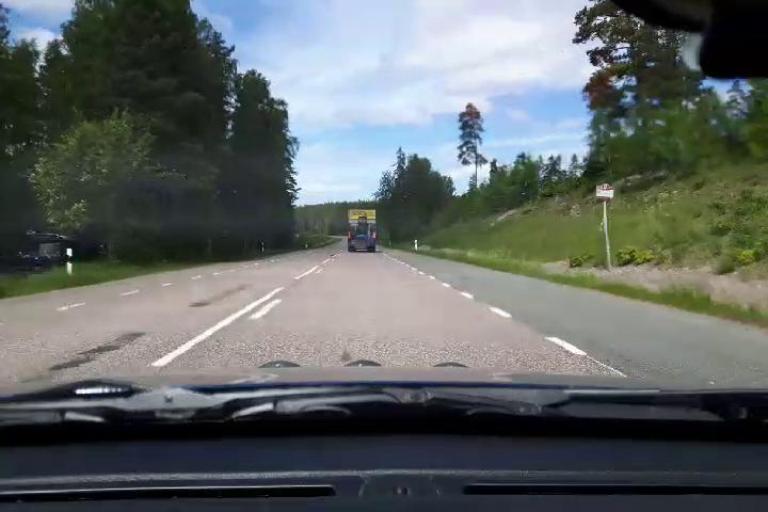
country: SE
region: Uppsala
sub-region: Osthammars Kommun
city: Bjorklinge
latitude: 60.0965
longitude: 17.5539
